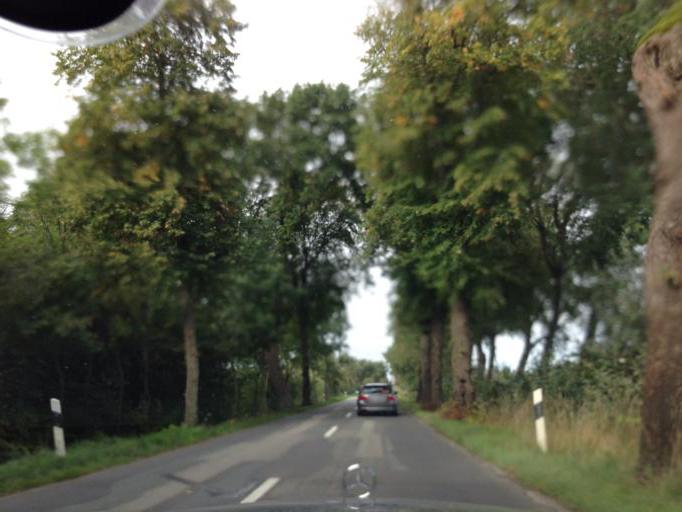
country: DE
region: Schleswig-Holstein
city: Galmsbull
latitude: 54.7687
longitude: 8.7513
